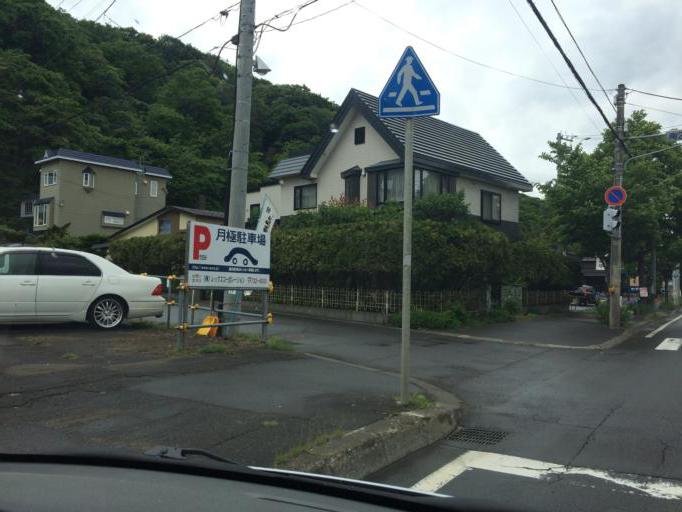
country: JP
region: Hokkaido
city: Sapporo
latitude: 43.0252
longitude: 141.3410
